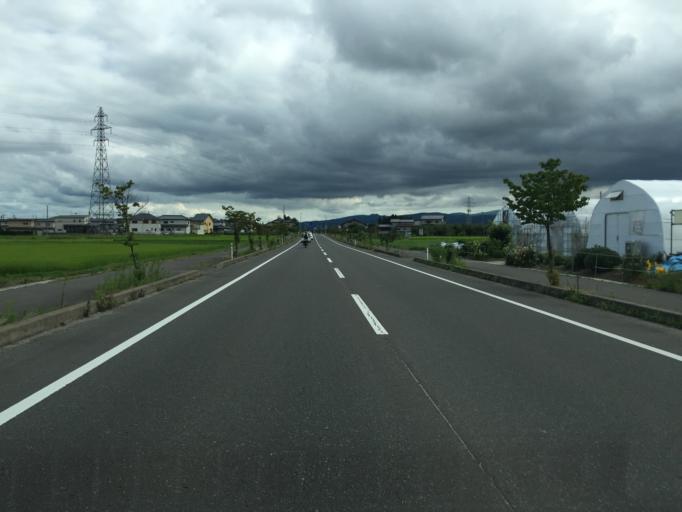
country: JP
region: Fukushima
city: Fukushima-shi
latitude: 37.7938
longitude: 140.4284
